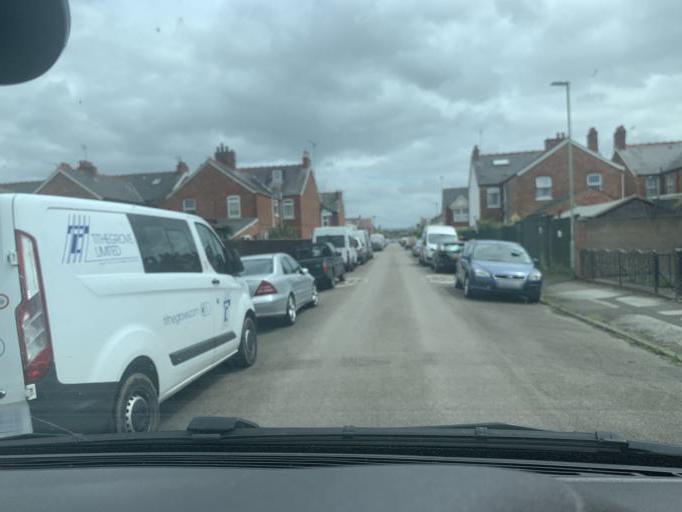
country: GB
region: England
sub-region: Gloucestershire
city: Gloucester
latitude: 51.8537
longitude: -2.2481
